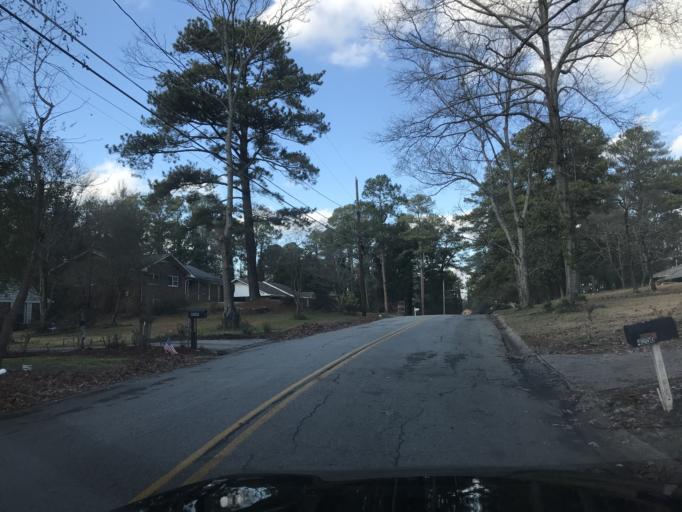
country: US
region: Georgia
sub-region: Fulton County
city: College Park
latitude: 33.6395
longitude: -84.4766
